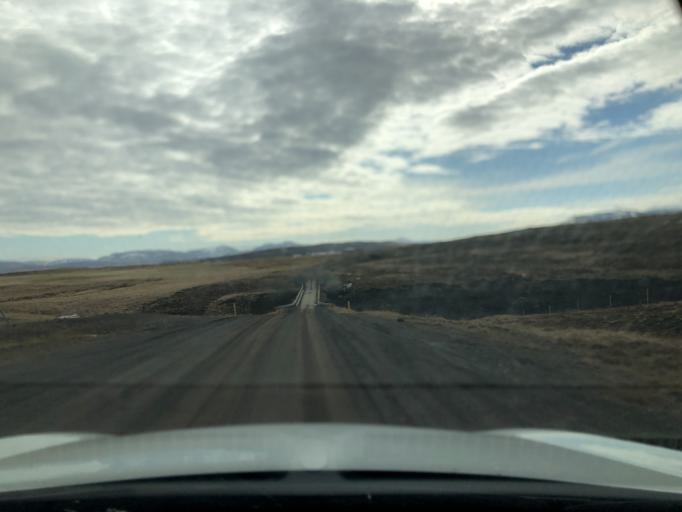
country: IS
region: West
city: Borgarnes
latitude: 65.0116
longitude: -21.9442
